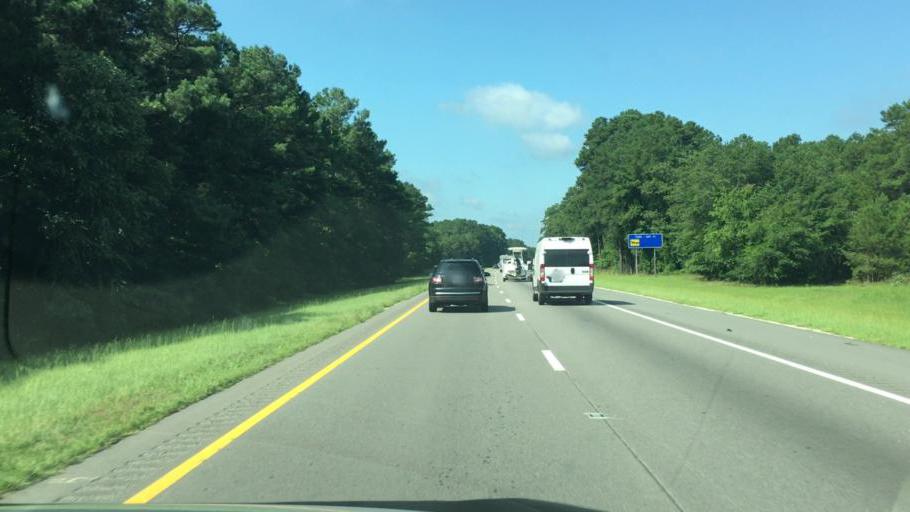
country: US
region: North Carolina
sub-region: Cumberland County
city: Hope Mills
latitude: 34.9461
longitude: -78.9085
